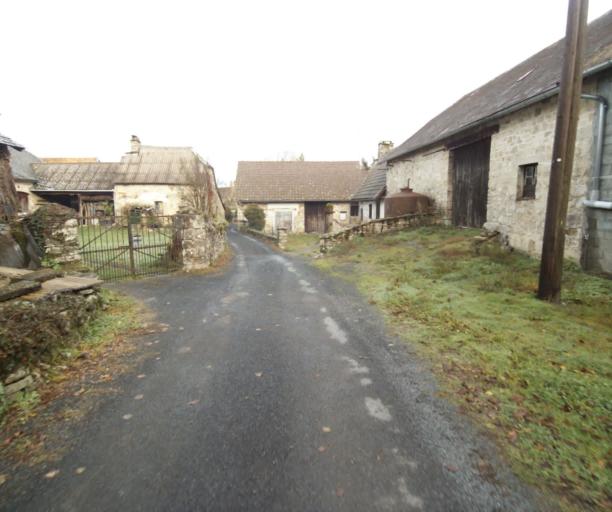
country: FR
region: Limousin
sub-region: Departement de la Correze
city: Cornil
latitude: 45.2118
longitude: 1.7157
